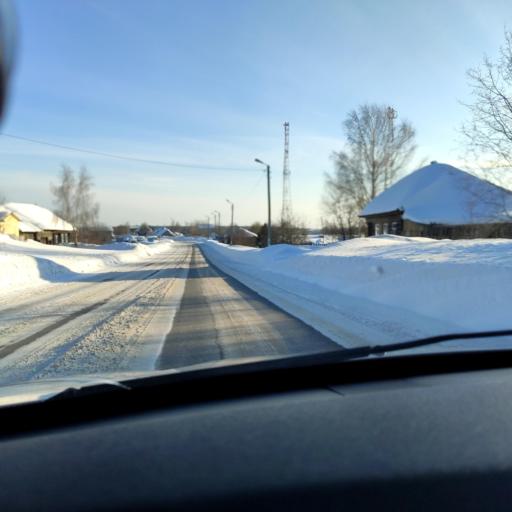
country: RU
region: Perm
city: Polazna
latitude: 58.3202
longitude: 56.4310
